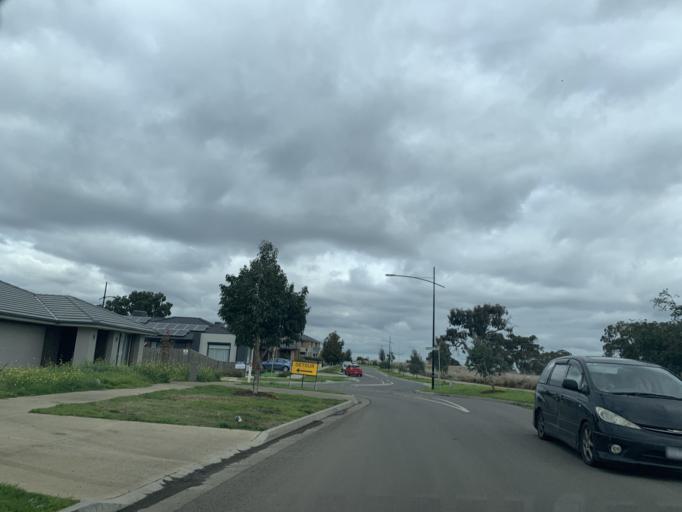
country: AU
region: Victoria
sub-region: Hume
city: Craigieburn
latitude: -37.6024
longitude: 144.9962
